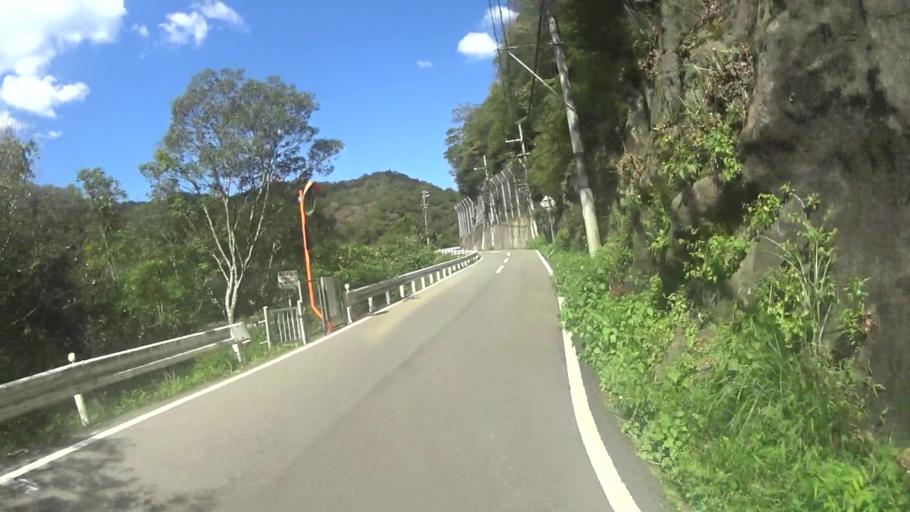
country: JP
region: Mie
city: Ueno-ebisumachi
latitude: 34.7623
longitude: 136.0061
